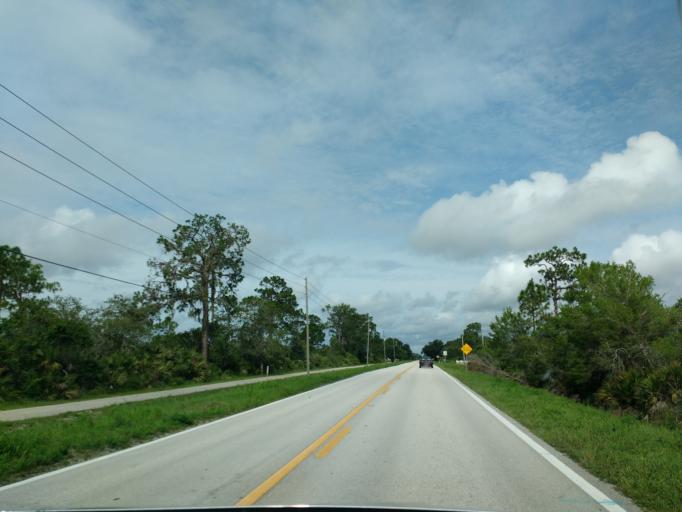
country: US
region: Florida
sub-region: Highlands County
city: Sebring
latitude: 27.4709
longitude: -81.4957
